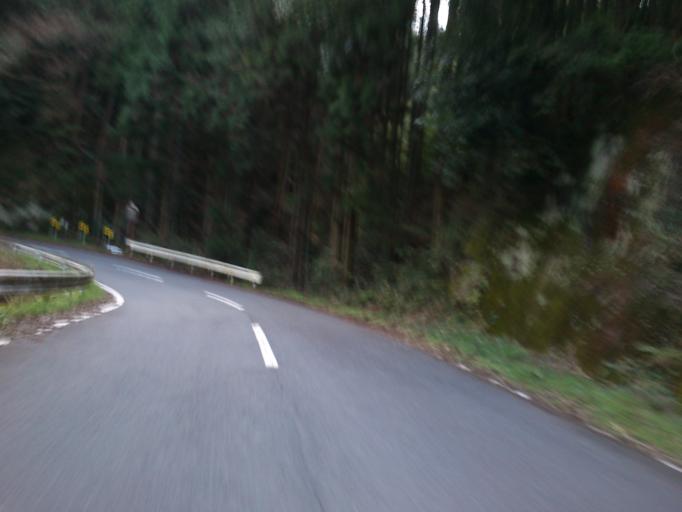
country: JP
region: Mie
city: Nabari
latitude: 34.7224
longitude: 136.0016
